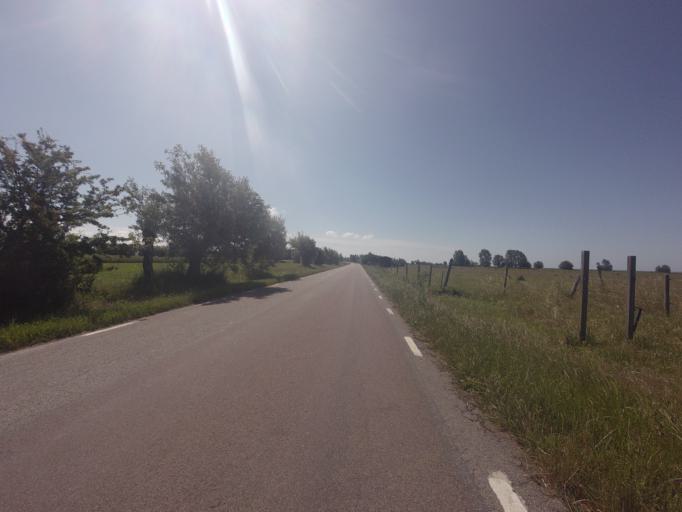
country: SE
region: Skane
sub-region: Malmo
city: Bunkeflostrand
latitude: 55.5071
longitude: 12.9397
